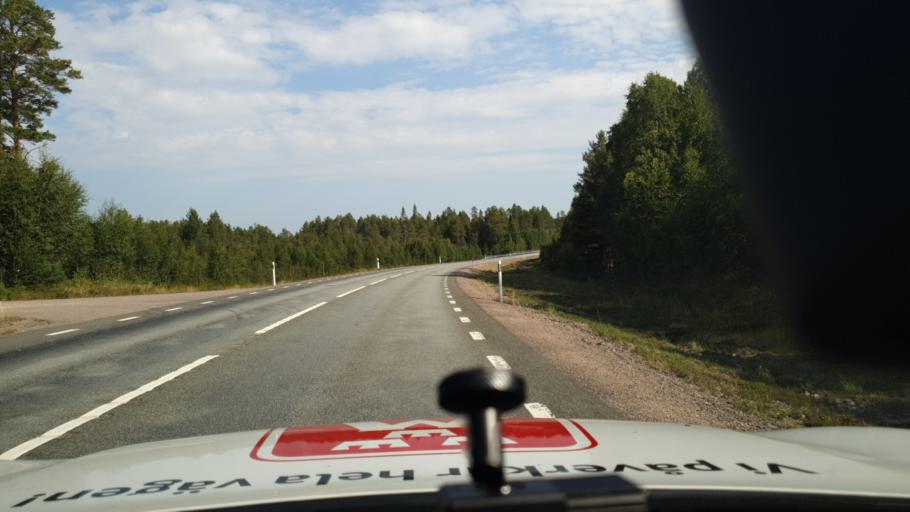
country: SE
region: Vaermland
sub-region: Hagfors Kommun
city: Ekshaerad
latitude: 60.4964
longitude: 13.4150
